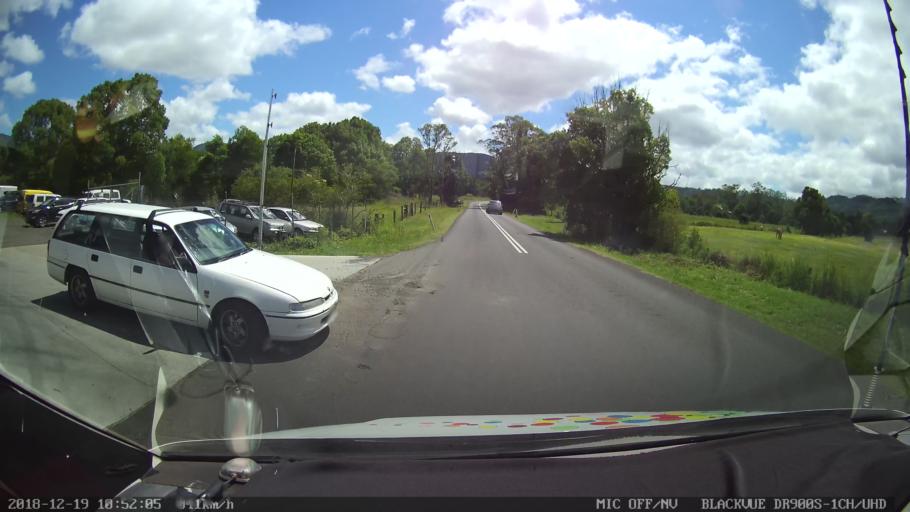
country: AU
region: New South Wales
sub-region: Lismore Municipality
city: Nimbin
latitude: -28.5933
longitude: 153.2270
